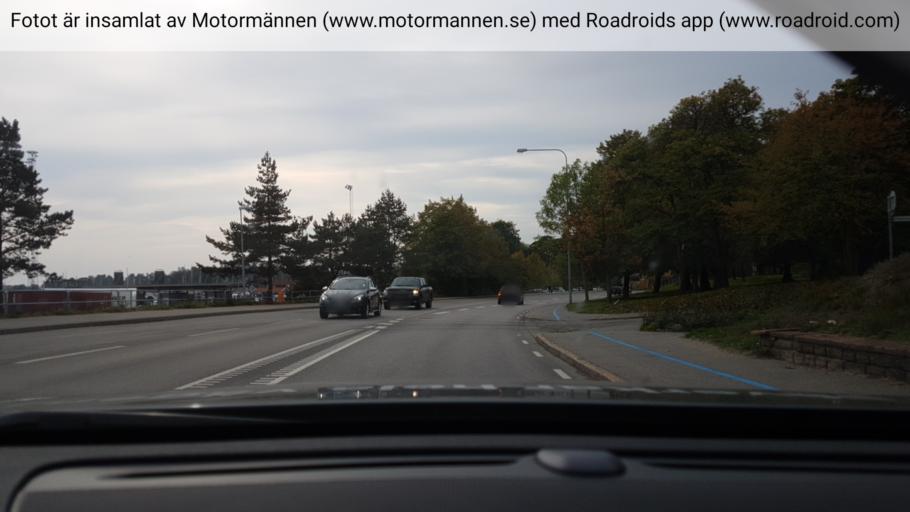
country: SE
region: Stockholm
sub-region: Nynashamns Kommun
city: Nynashamn
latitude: 58.9034
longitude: 17.9535
